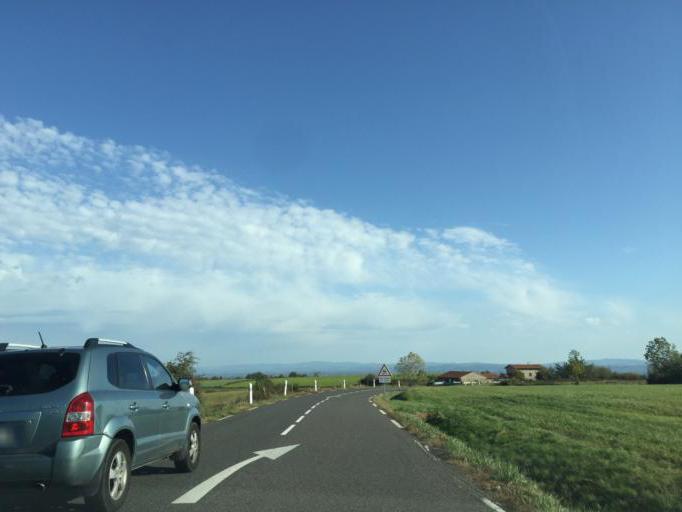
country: FR
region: Rhone-Alpes
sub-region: Departement de la Loire
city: Perigneux
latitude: 45.4681
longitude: 4.1306
